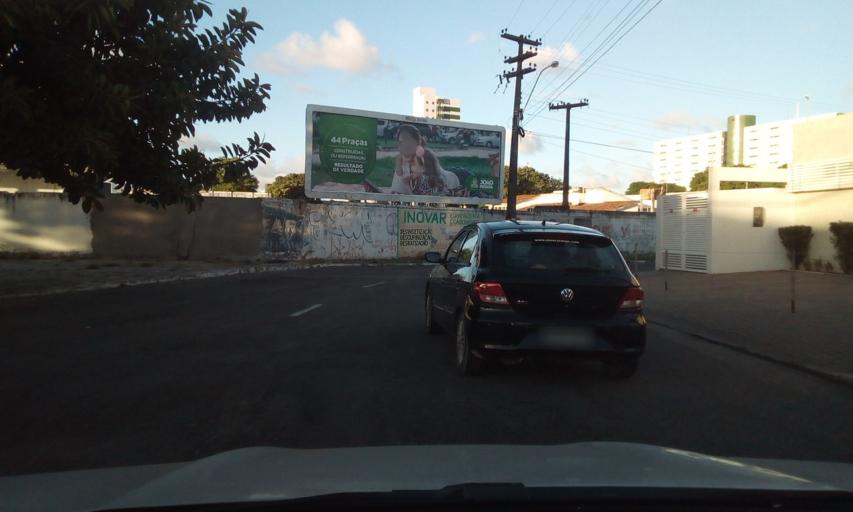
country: BR
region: Paraiba
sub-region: Joao Pessoa
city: Joao Pessoa
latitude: -7.1208
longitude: -34.8658
